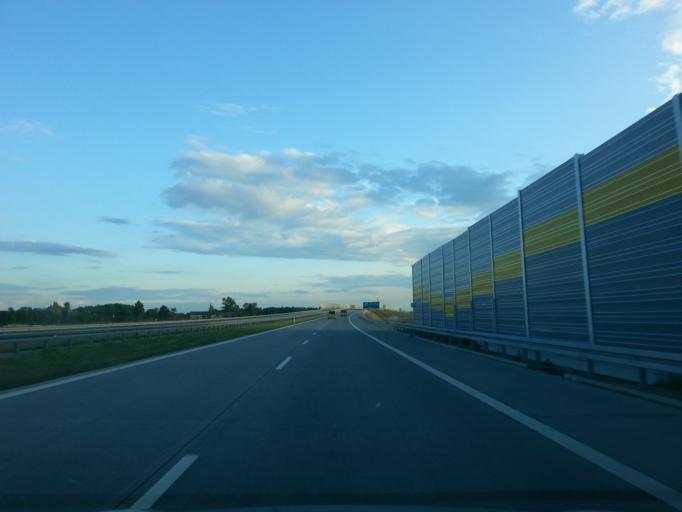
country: PL
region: Lodz Voivodeship
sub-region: Powiat sieradzki
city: Zloczew
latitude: 51.4126
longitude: 18.6388
